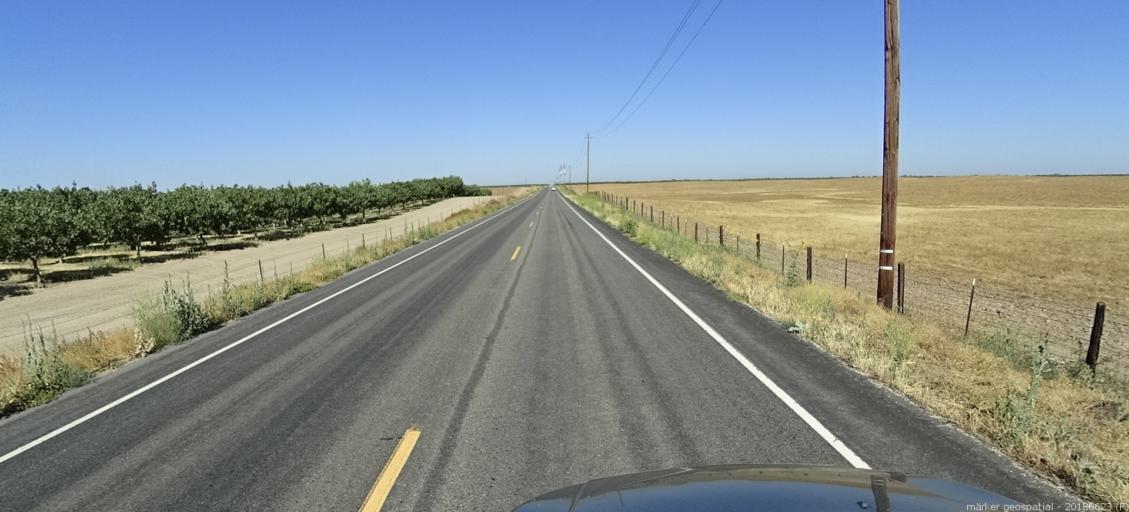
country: US
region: California
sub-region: Madera County
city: Bonadelle Ranchos-Madera Ranchos
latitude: 36.9666
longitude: -119.9323
